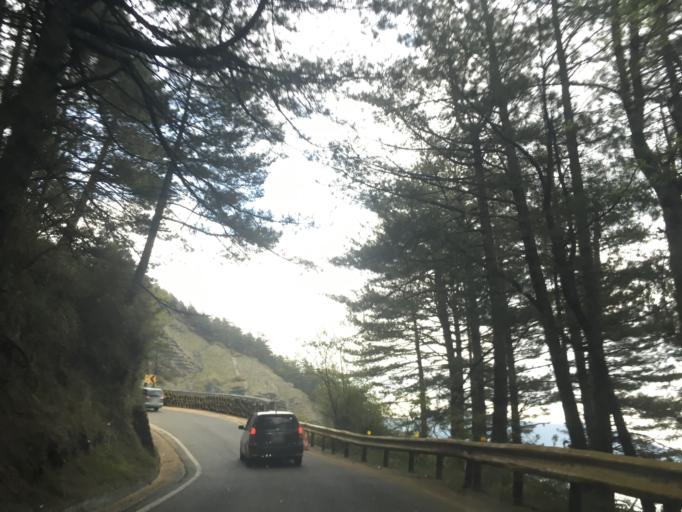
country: TW
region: Taiwan
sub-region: Hualien
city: Hualian
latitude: 24.1779
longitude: 121.3034
